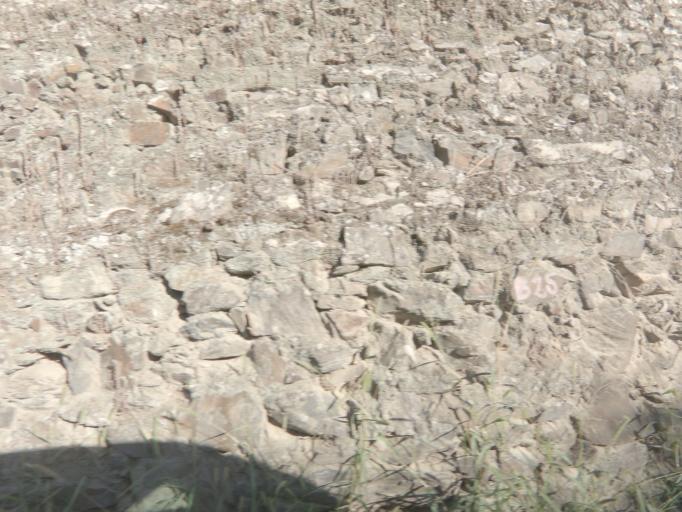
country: PT
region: Vila Real
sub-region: Peso da Regua
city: Peso da Regua
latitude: 41.1696
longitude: -7.7818
